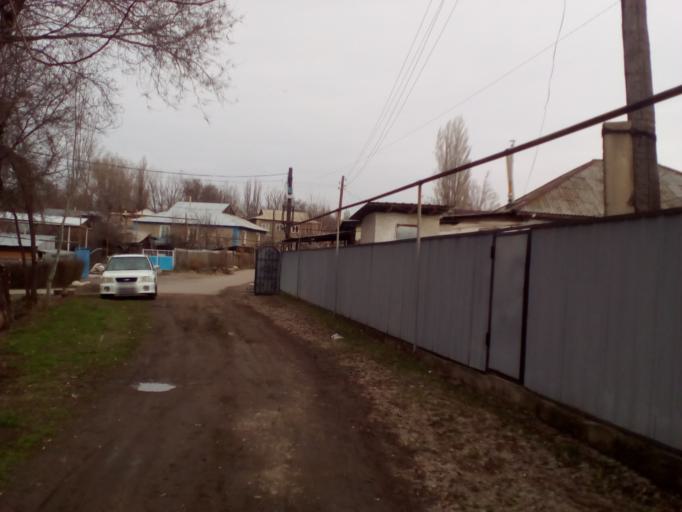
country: KZ
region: Almaty Oblysy
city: Burunday
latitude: 43.1567
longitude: 76.4098
